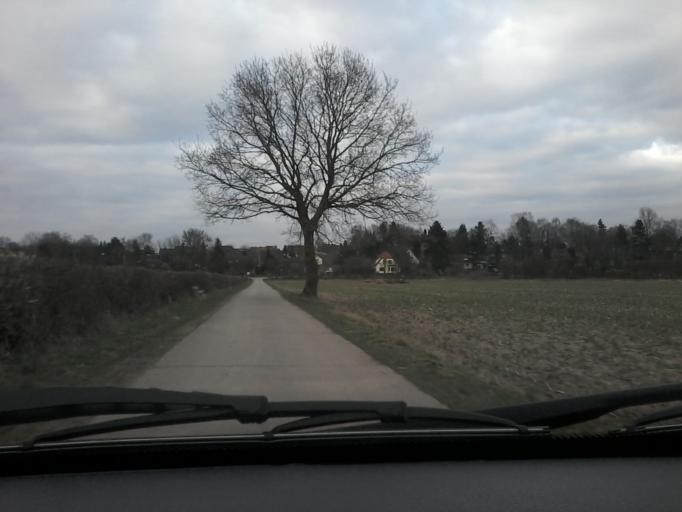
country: DE
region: Lower Saxony
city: Achim
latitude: 52.9995
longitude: 9.0381
